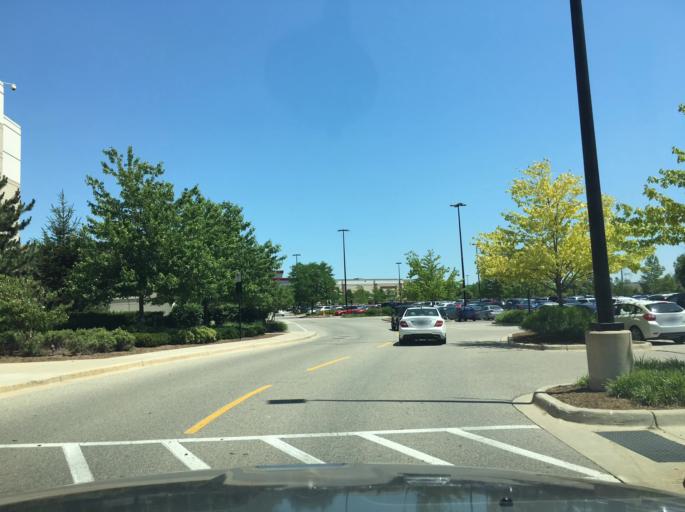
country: US
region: Michigan
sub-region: Macomb County
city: Clinton
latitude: 42.6249
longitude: -82.9490
